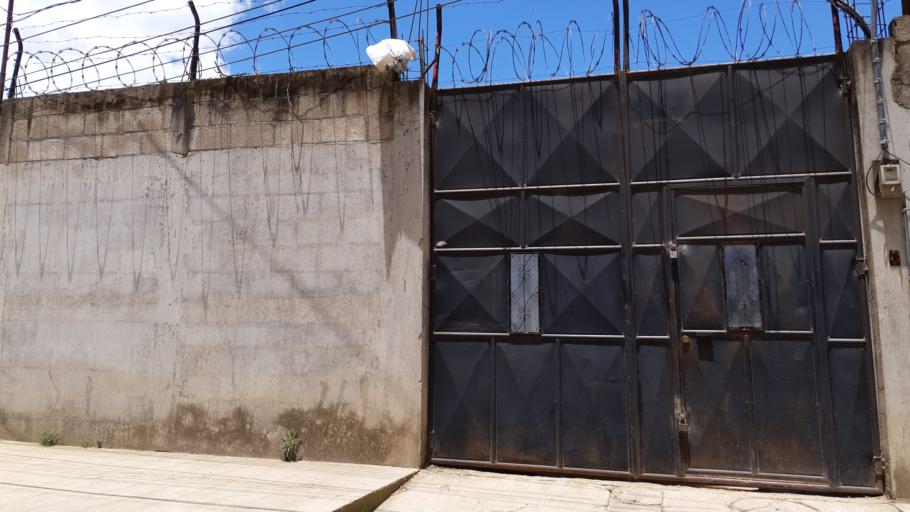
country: GT
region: Chimaltenango
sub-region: Municipio de Chimaltenango
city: Chimaltenango
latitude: 14.6646
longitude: -90.8471
